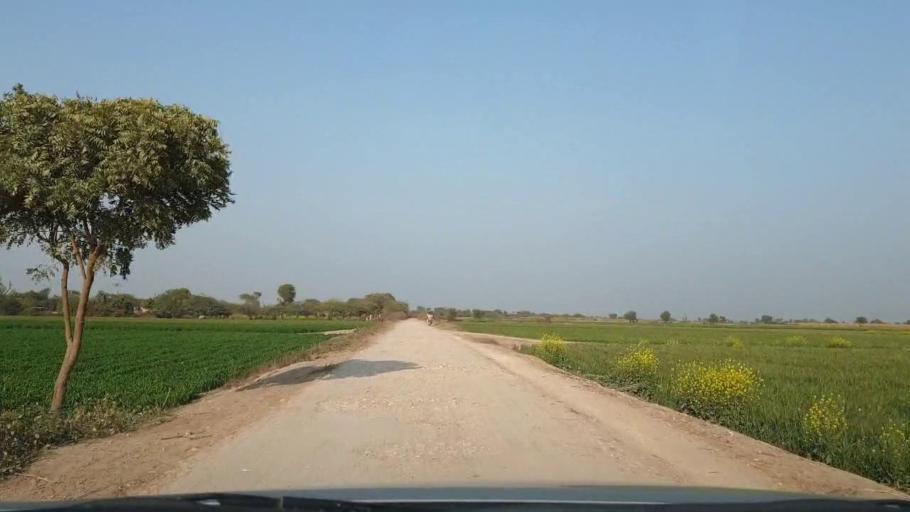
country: PK
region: Sindh
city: Tando Adam
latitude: 25.6689
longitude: 68.6360
